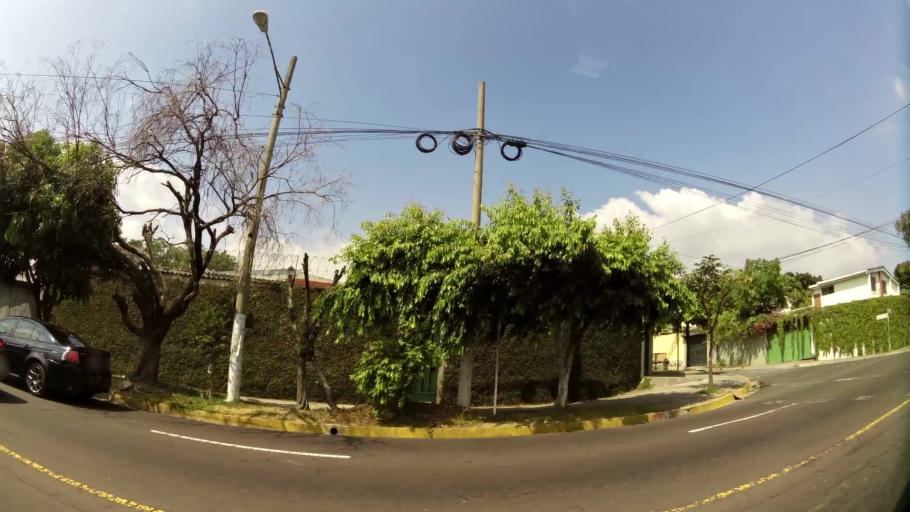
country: SV
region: San Salvador
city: Mejicanos
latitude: 13.7103
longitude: -89.2196
